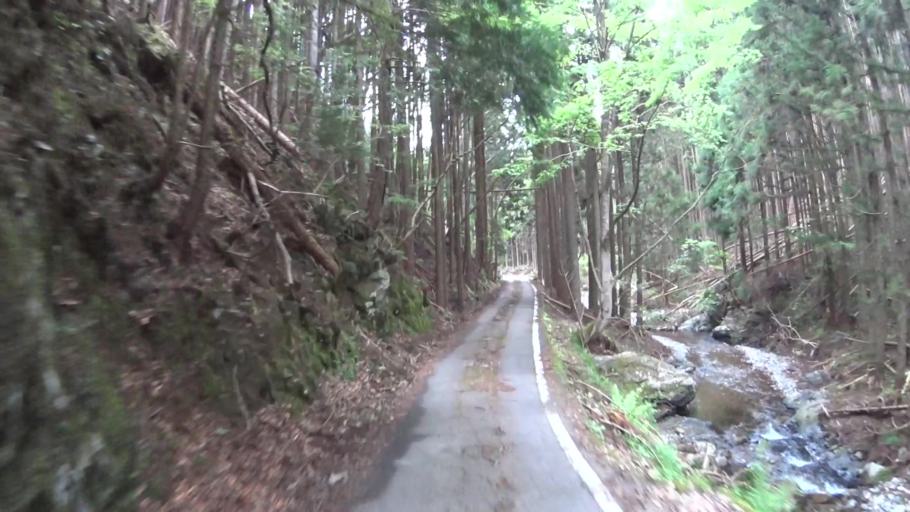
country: JP
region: Kyoto
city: Kameoka
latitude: 35.1078
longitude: 135.6328
